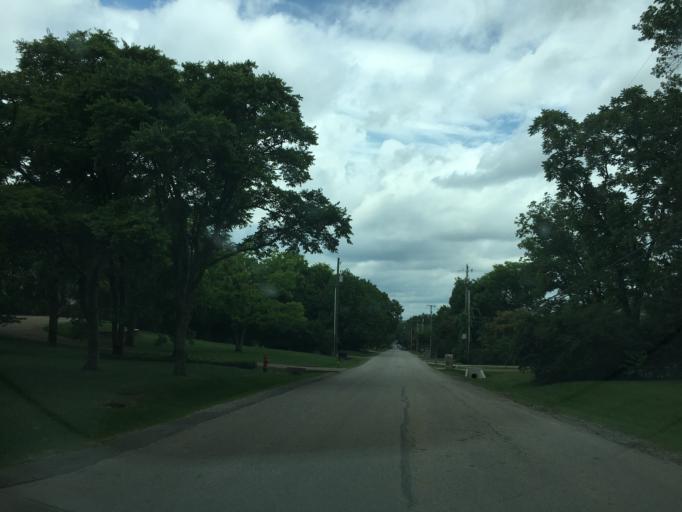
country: US
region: Tennessee
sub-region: Davidson County
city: Belle Meade
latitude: 36.0954
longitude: -86.8348
